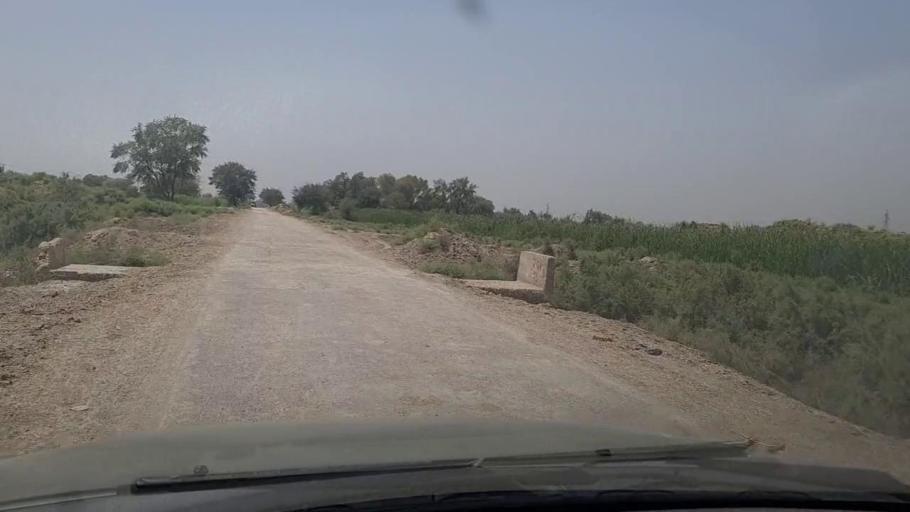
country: PK
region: Sindh
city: Ratodero
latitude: 27.7876
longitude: 68.2082
